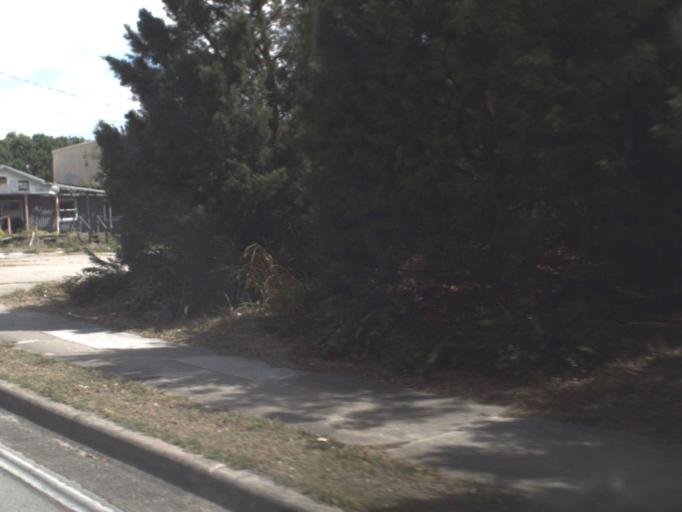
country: US
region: Florida
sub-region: Brevard County
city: Cocoa West
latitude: 28.3615
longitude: -80.7549
